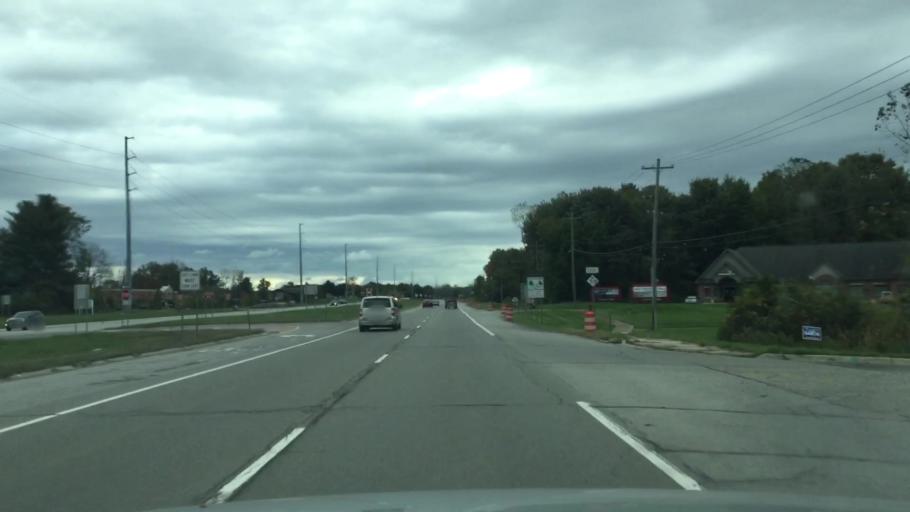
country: US
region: Michigan
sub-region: Livingston County
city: Brighton
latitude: 42.6349
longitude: -83.7369
